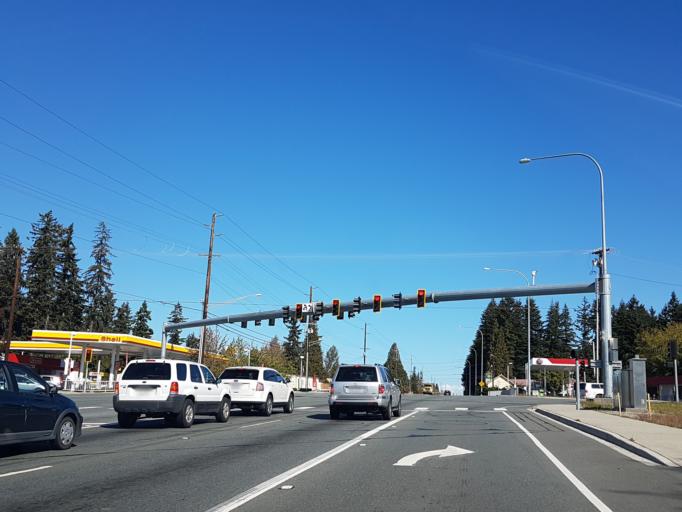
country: US
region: Washington
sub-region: Snohomish County
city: Clearview
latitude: 47.8332
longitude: -122.1263
